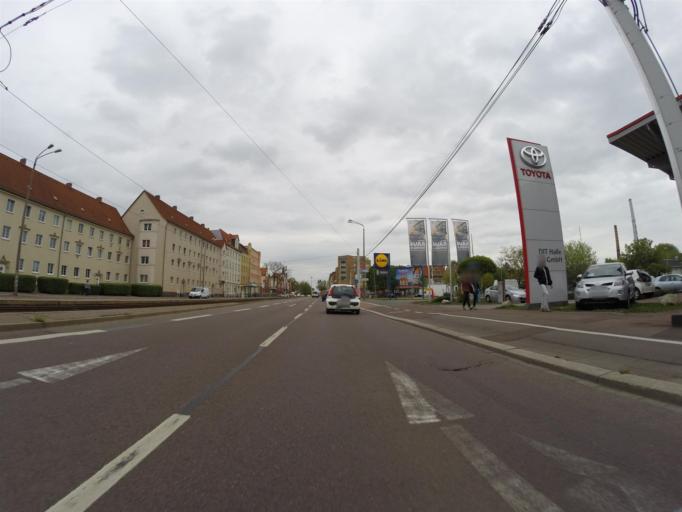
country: DE
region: Saxony-Anhalt
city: Halle (Saale)
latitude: 51.4557
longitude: 11.9839
